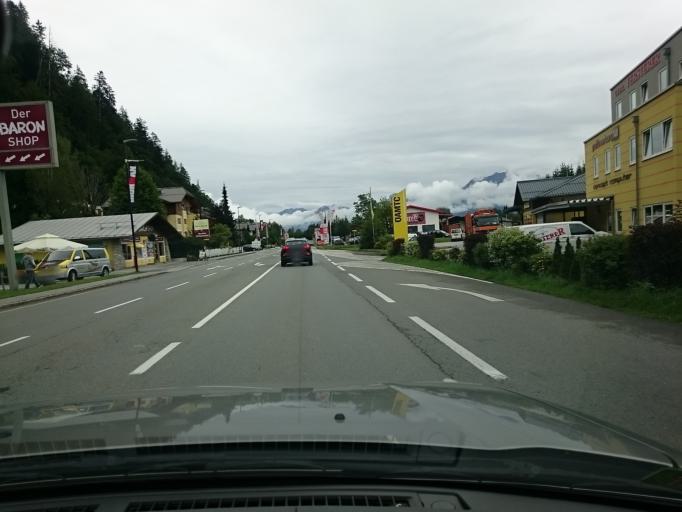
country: AT
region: Salzburg
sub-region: Politischer Bezirk Zell am See
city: Zell am See
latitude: 47.3399
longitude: 12.7979
